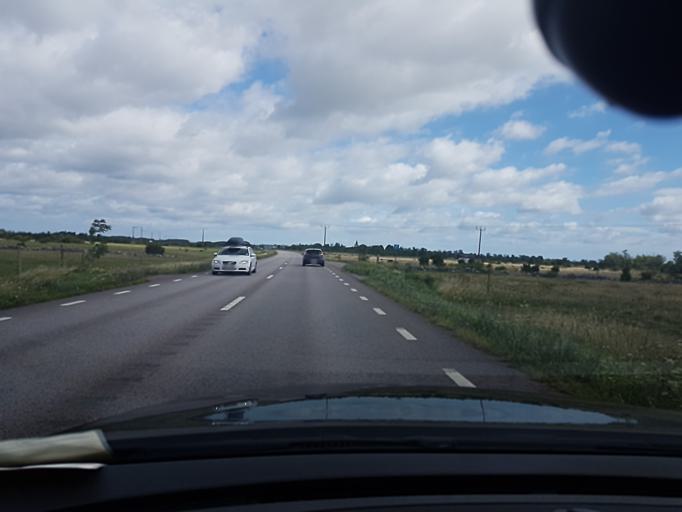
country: SE
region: Kalmar
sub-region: Borgholms Kommun
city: Borgholm
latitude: 56.9375
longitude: 16.7741
